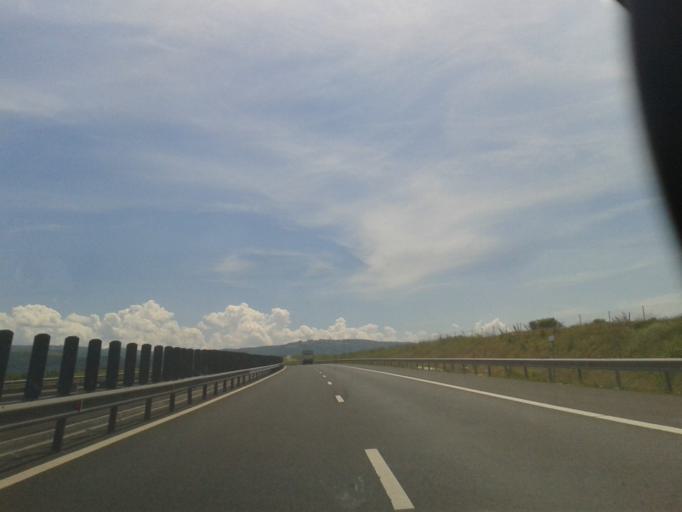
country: RO
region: Sibiu
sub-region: Comuna Apoldu de Jos
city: Apoldu de Jos
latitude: 45.8423
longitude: 23.8654
